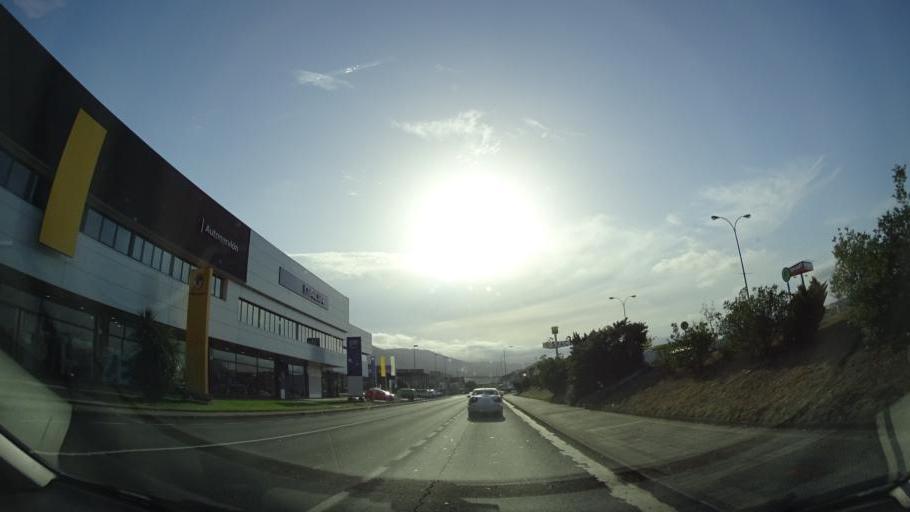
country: ES
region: Basque Country
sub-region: Bizkaia
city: Barakaldo
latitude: 43.2987
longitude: -3.0040
